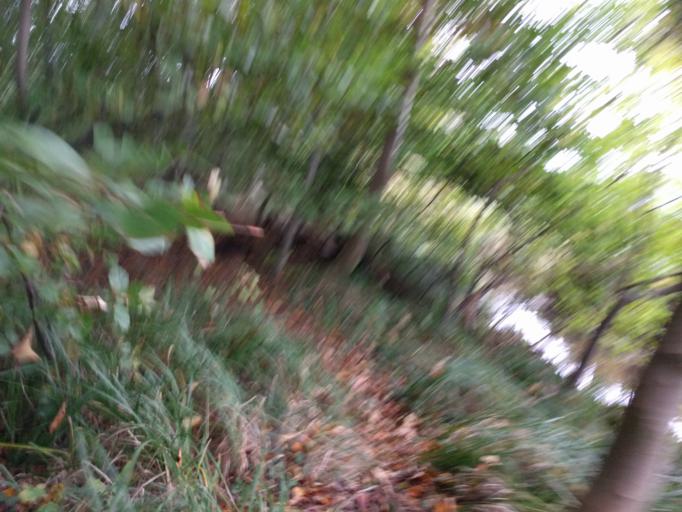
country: DK
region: South Denmark
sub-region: Kerteminde Kommune
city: Langeskov
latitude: 55.3995
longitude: 10.5661
